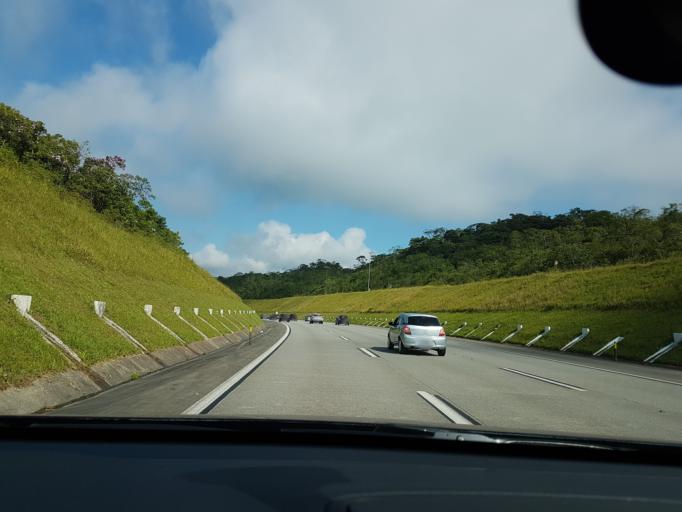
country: BR
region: Sao Paulo
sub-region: Cubatao
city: Cubatao
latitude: -23.9275
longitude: -46.5527
